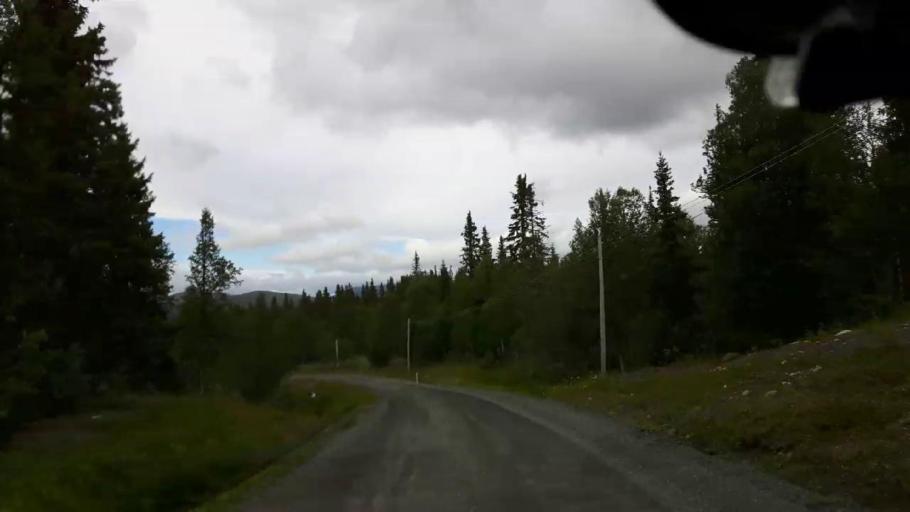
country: SE
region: Jaemtland
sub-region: Krokoms Kommun
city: Valla
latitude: 63.7781
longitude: 13.8296
